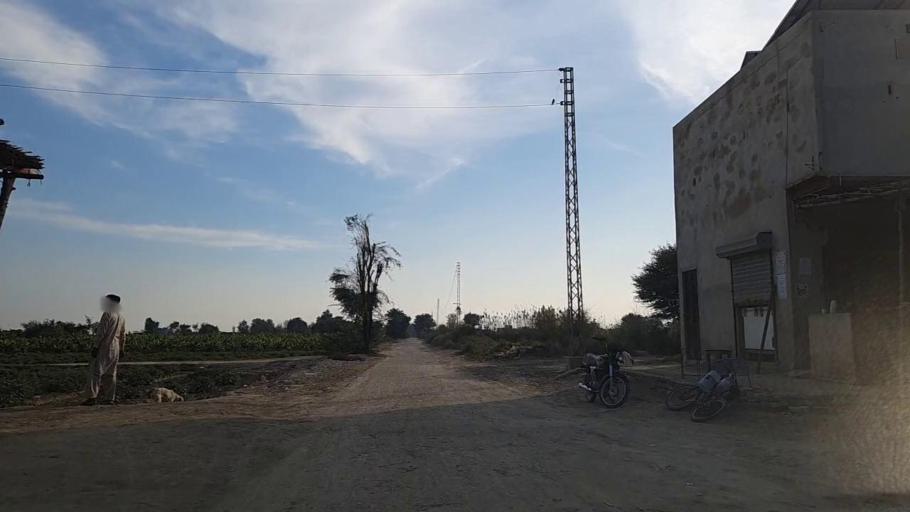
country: PK
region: Sindh
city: Bandhi
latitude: 26.5664
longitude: 68.2787
